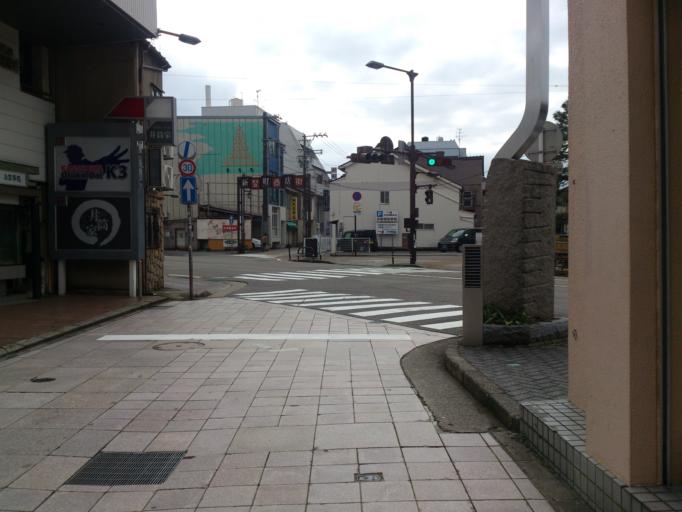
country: JP
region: Ishikawa
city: Nonoichi
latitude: 36.5575
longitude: 136.6554
